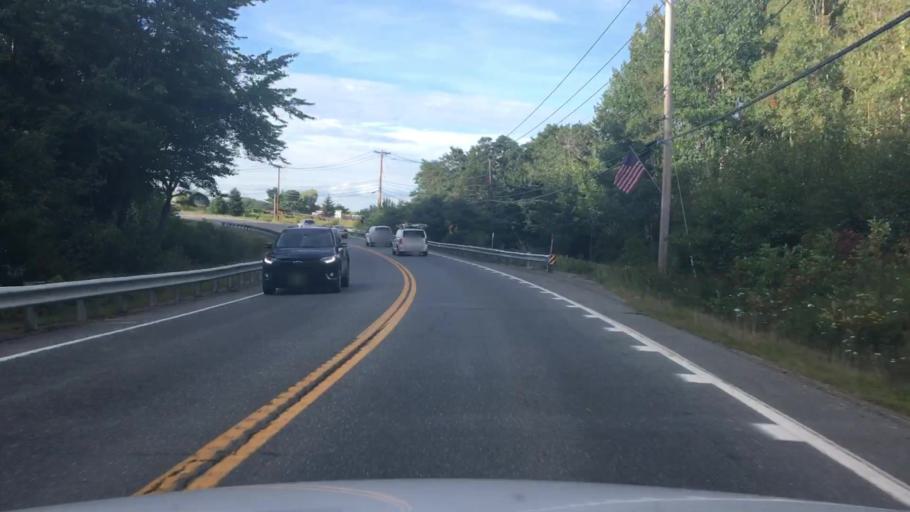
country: US
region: Maine
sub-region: Hancock County
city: Trenton
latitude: 44.4817
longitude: -68.3657
